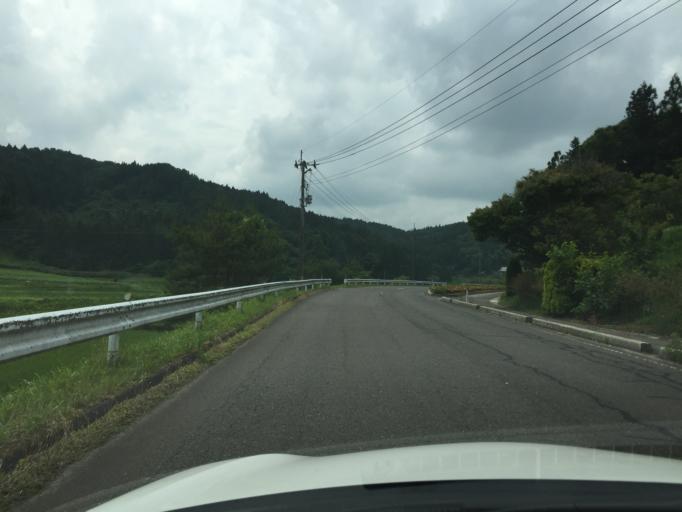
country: JP
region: Fukushima
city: Funehikimachi-funehiki
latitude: 37.2990
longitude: 140.5652
